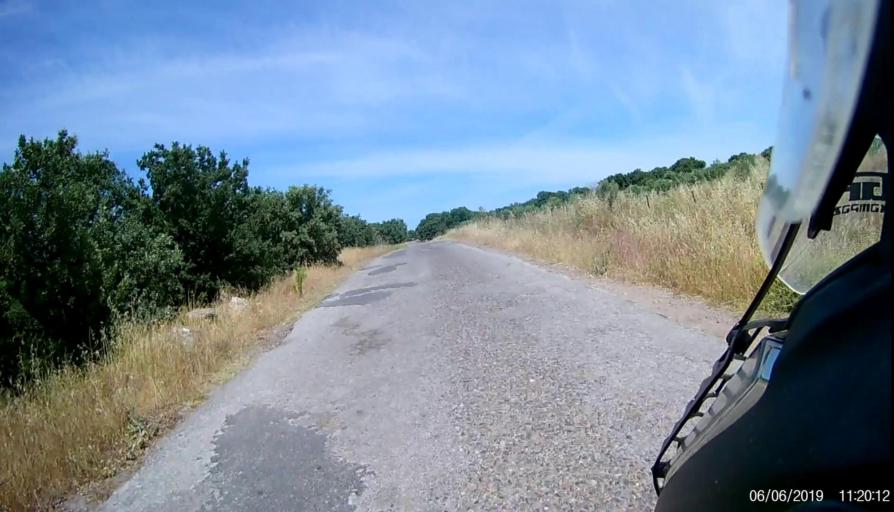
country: TR
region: Canakkale
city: Gulpinar
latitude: 39.6639
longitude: 26.1638
